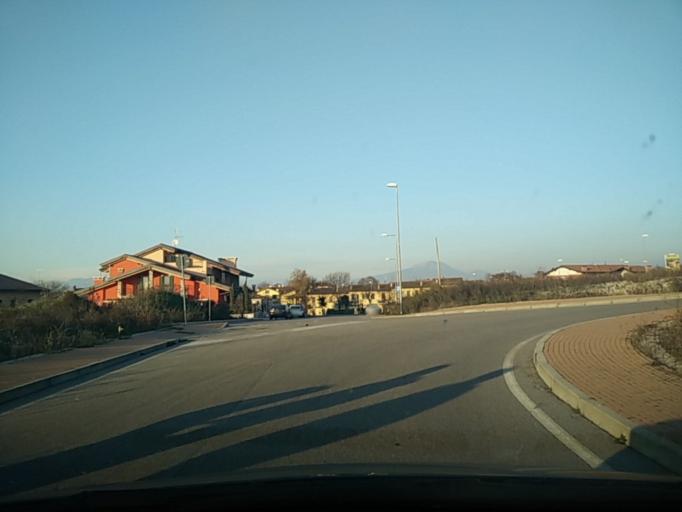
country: IT
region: Veneto
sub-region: Provincia di Verona
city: Salionze
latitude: 45.4021
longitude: 10.7251
